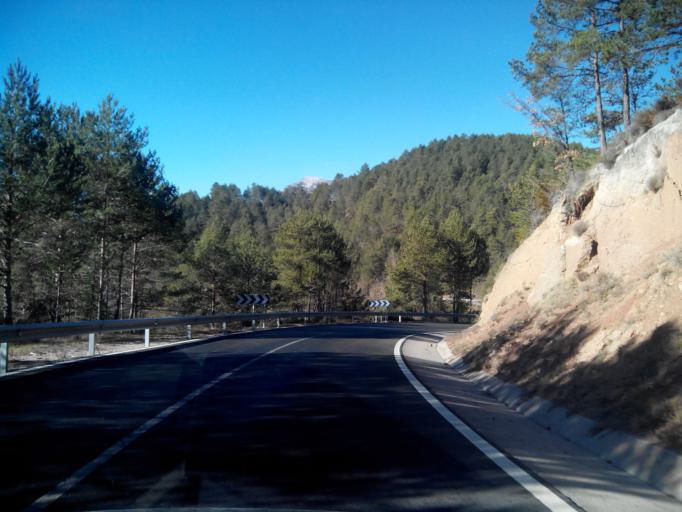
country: ES
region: Catalonia
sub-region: Provincia de Barcelona
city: Capolat
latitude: 42.1268
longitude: 1.6663
